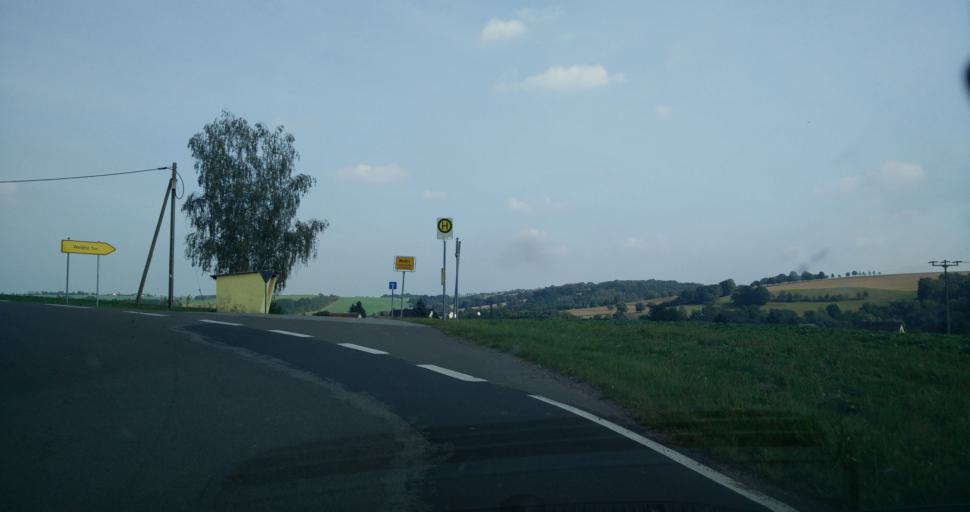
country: DE
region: Saxony
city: Rochlitz
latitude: 51.0804
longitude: 12.7921
